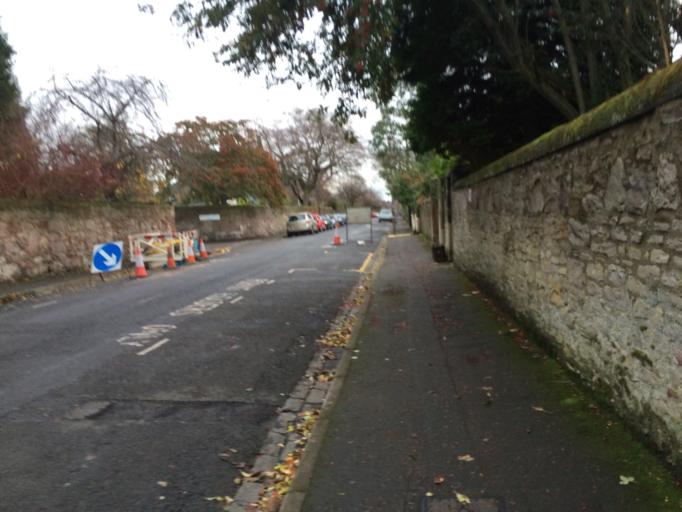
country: GB
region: Scotland
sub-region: Edinburgh
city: Edinburgh
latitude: 55.9335
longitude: -3.1880
